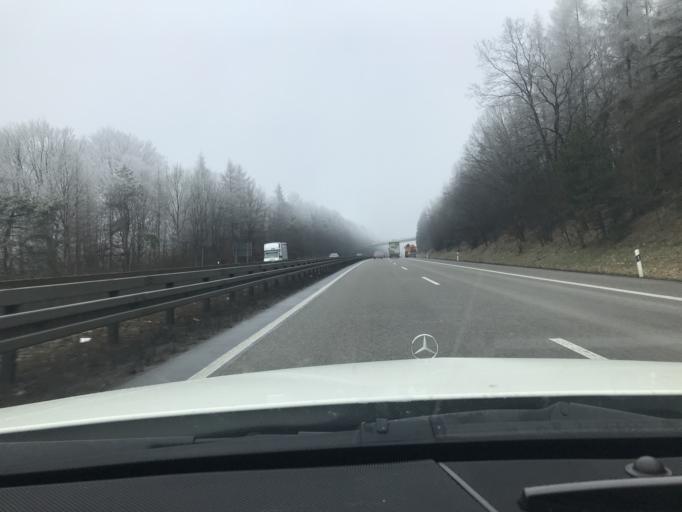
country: DE
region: Bavaria
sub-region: Regierungsbezirk Unterfranken
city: Motten
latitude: 50.3631
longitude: 9.7335
